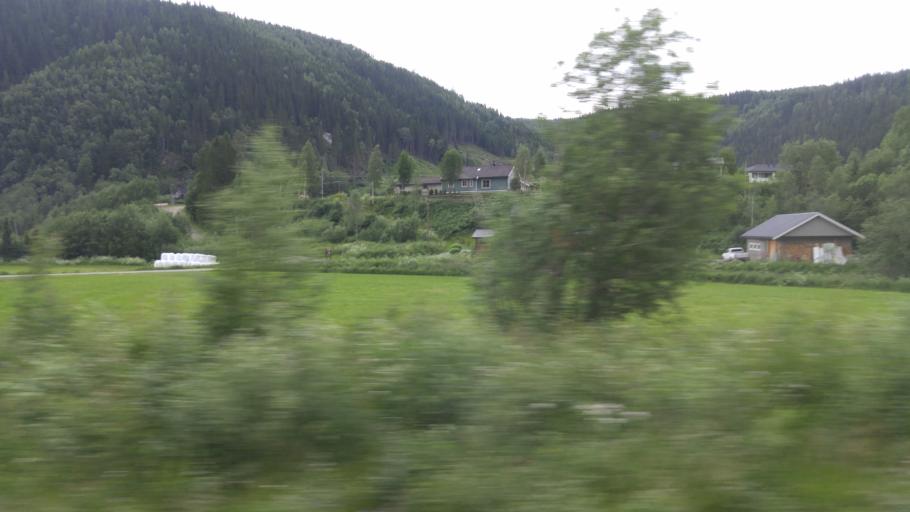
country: NO
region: Nord-Trondelag
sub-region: Levanger
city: Skogn
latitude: 63.4582
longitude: 11.3501
